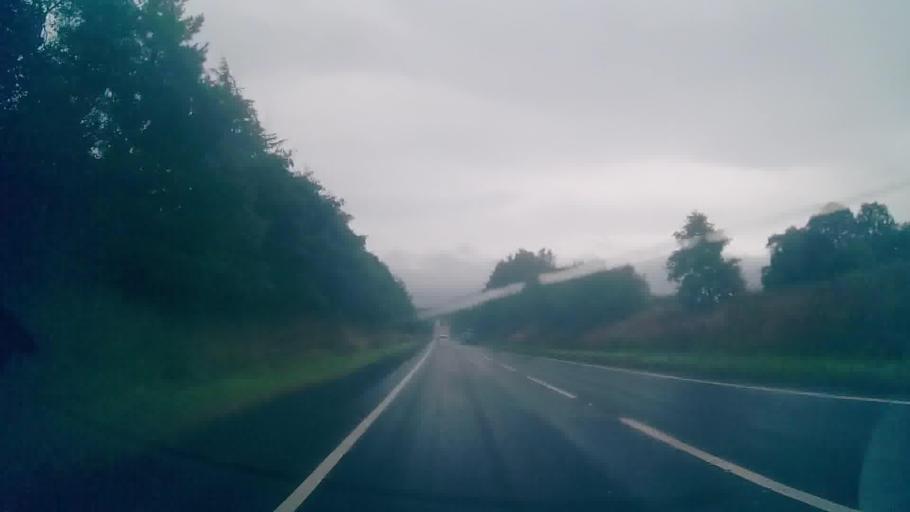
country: GB
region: Scotland
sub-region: East Ayrshire
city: Auchinleck
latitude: 55.4663
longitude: -4.3024
